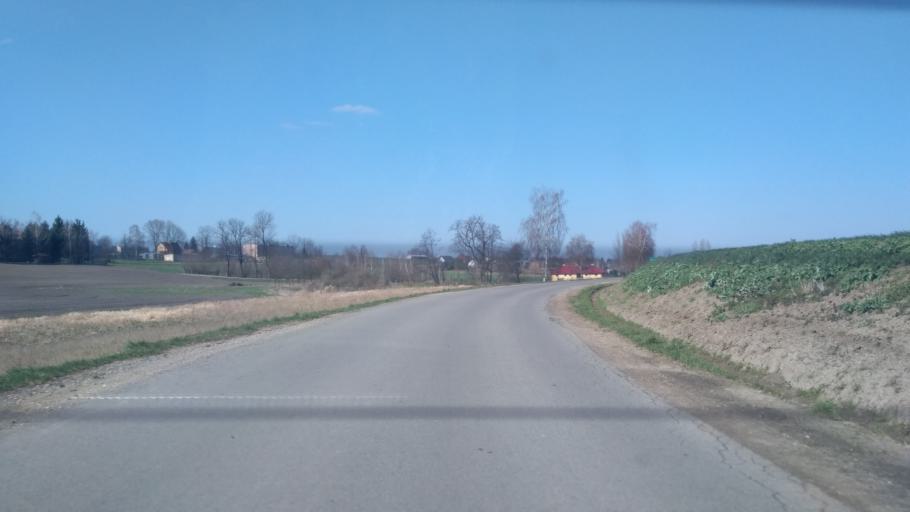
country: PL
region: Subcarpathian Voivodeship
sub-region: Powiat jaroslawski
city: Pawlosiow
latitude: 49.9536
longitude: 22.6574
